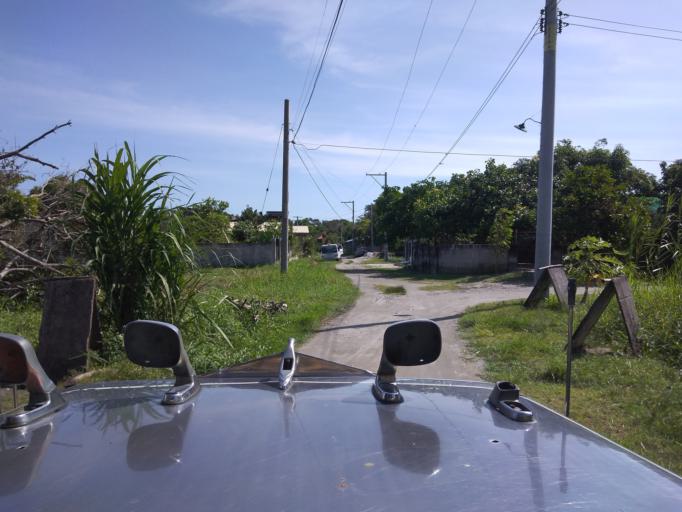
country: PH
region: Central Luzon
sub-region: Province of Pampanga
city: Bacolor
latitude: 15.0038
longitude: 120.6699
